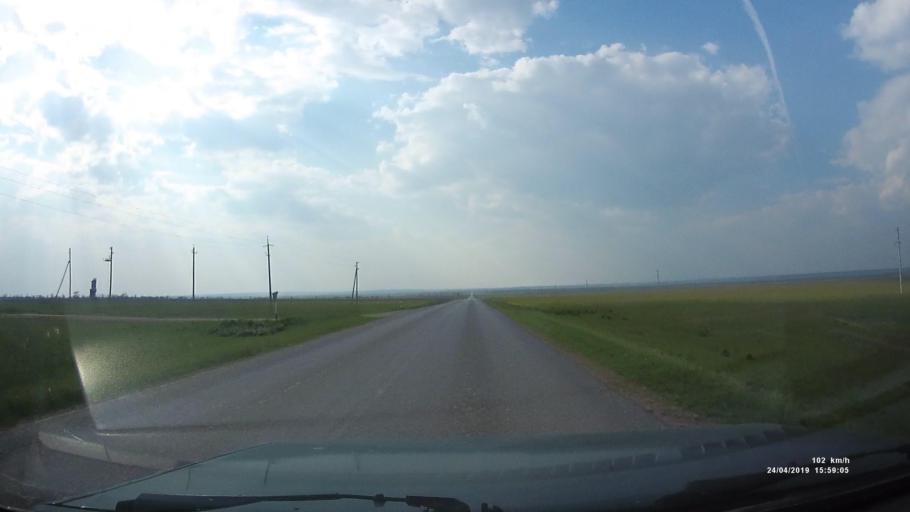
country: RU
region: Kalmykiya
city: Yashalta
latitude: 46.6200
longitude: 42.4786
